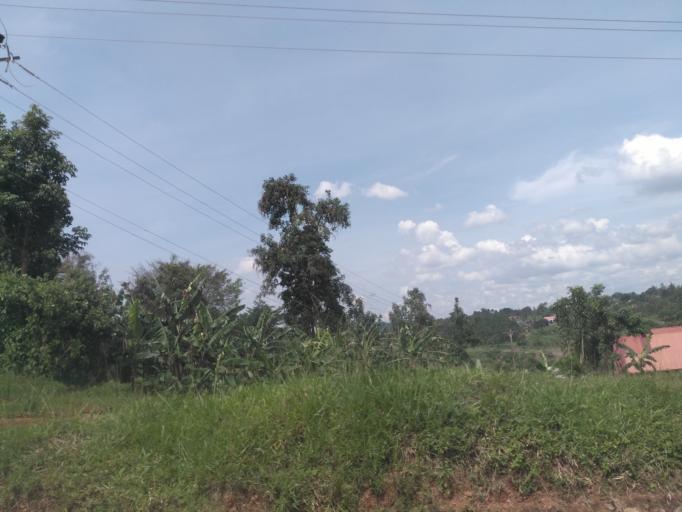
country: UG
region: Central Region
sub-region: Wakiso District
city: Bweyogerere
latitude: 0.4752
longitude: 32.6071
